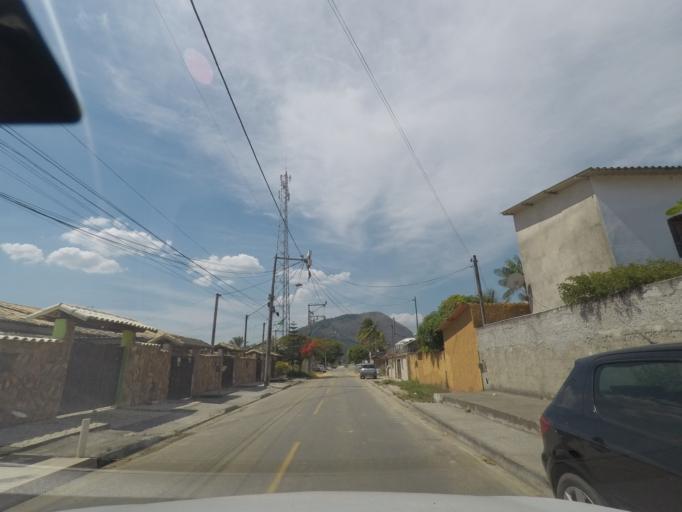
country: BR
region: Rio de Janeiro
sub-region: Marica
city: Marica
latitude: -22.9615
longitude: -42.9640
